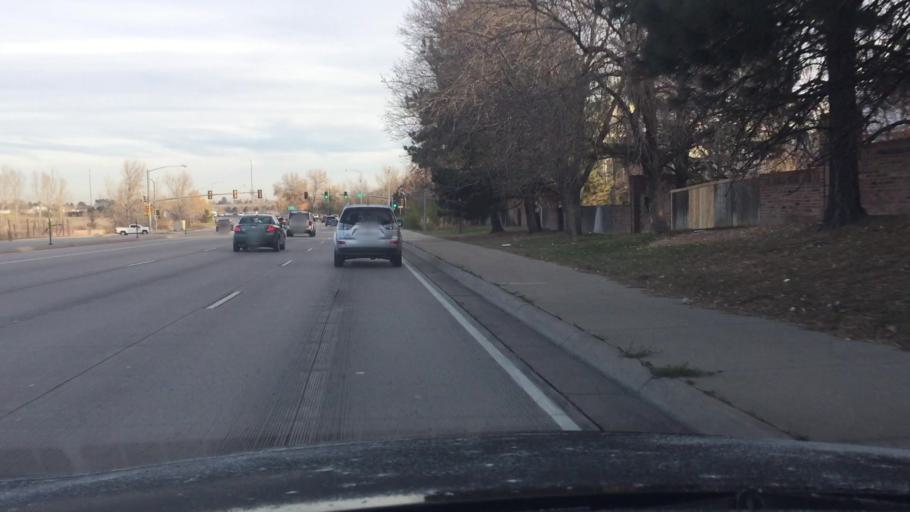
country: US
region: Colorado
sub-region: Arapahoe County
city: Dove Valley
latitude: 39.6459
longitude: -104.8287
